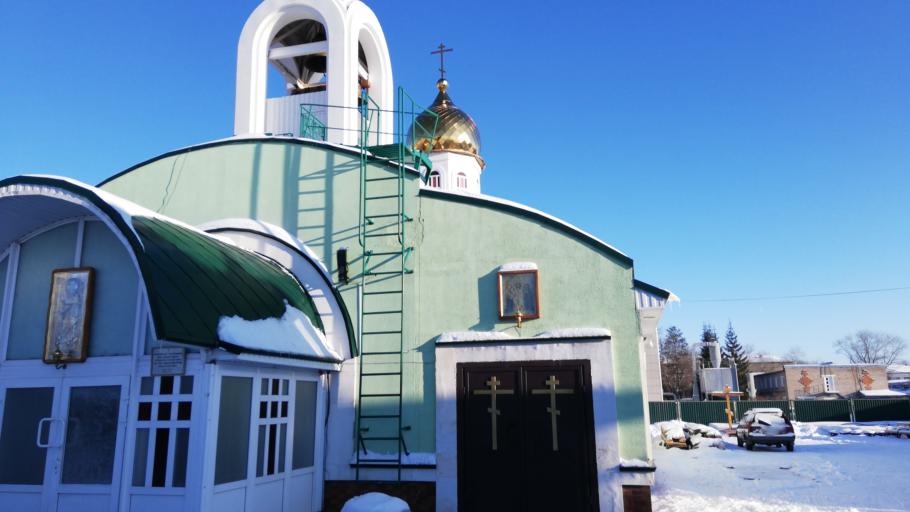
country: KZ
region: Soltustik Qazaqstan
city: Petropavlovsk
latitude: 54.8585
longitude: 69.1600
